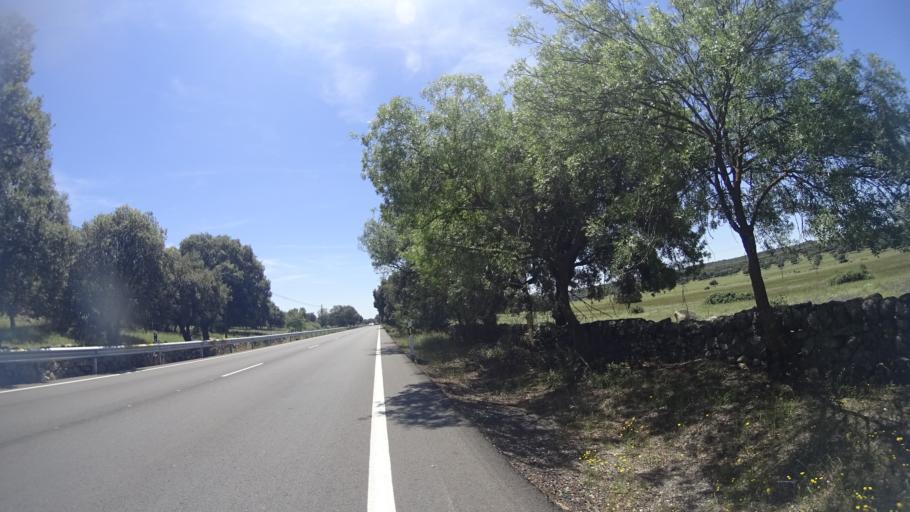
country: ES
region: Madrid
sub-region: Provincia de Madrid
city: Galapagar
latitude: 40.5981
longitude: -4.0176
